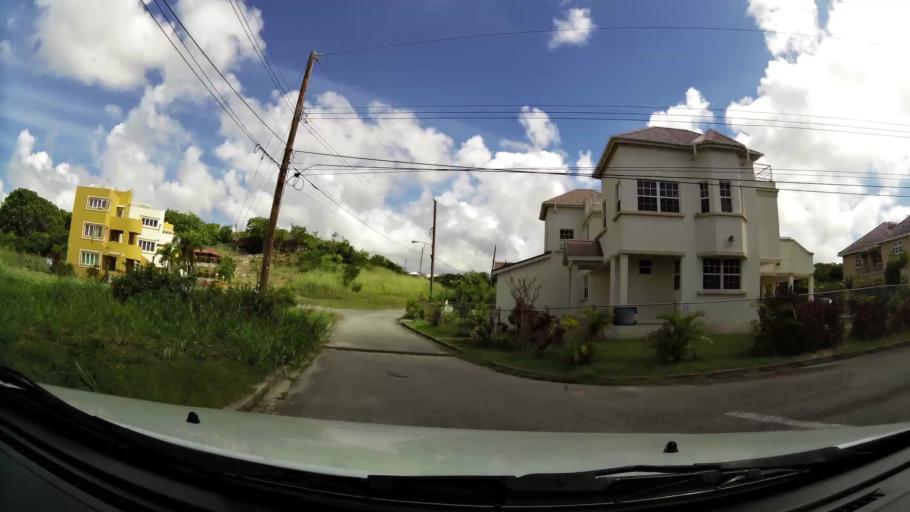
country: BB
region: Saint James
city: Holetown
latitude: 13.1441
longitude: -59.6283
